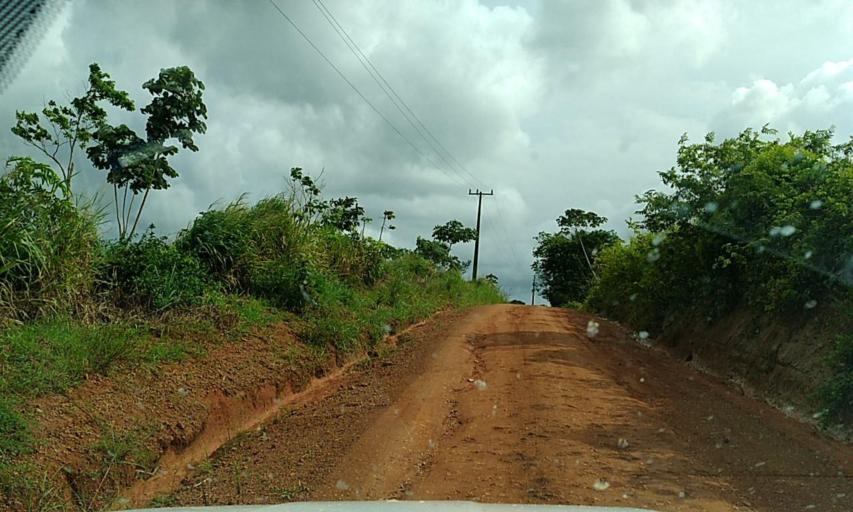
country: BR
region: Para
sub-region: Altamira
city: Altamira
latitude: -3.3133
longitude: -52.6849
